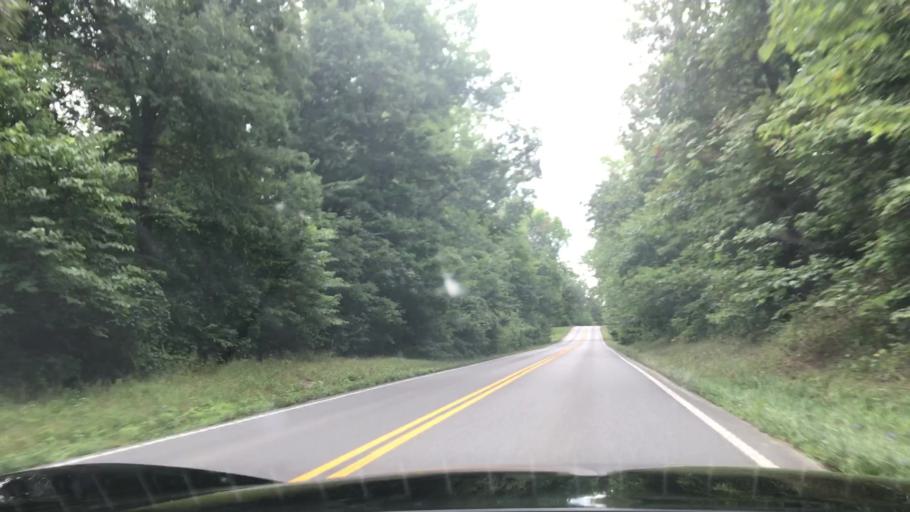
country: US
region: Kentucky
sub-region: Muhlenberg County
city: Central City
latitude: 37.2105
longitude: -87.0428
